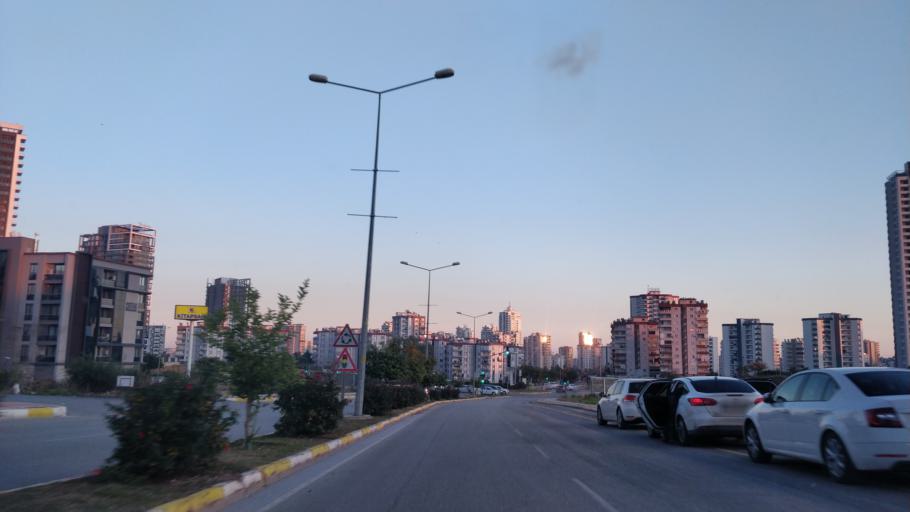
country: TR
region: Mersin
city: Mercin
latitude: 36.7982
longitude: 34.5765
